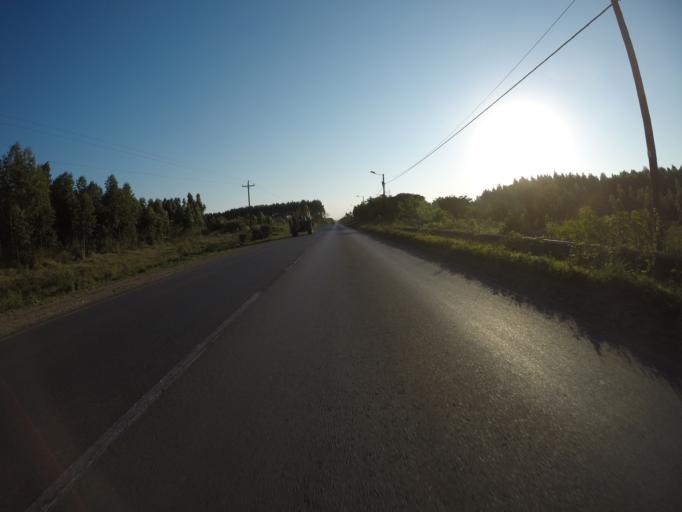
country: ZA
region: KwaZulu-Natal
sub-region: uThungulu District Municipality
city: KwaMbonambi
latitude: -28.6830
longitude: 32.1954
